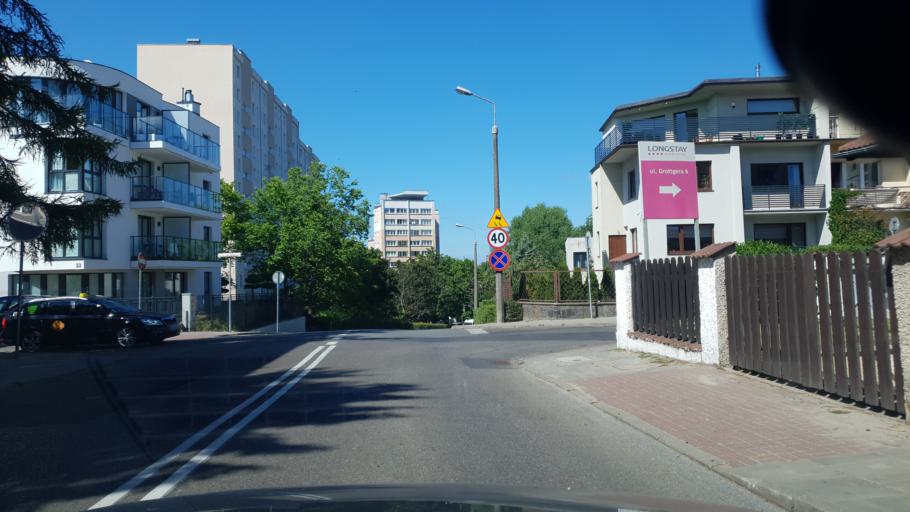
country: PL
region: Pomeranian Voivodeship
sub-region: Gdynia
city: Gdynia
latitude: 54.5050
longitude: 18.5430
